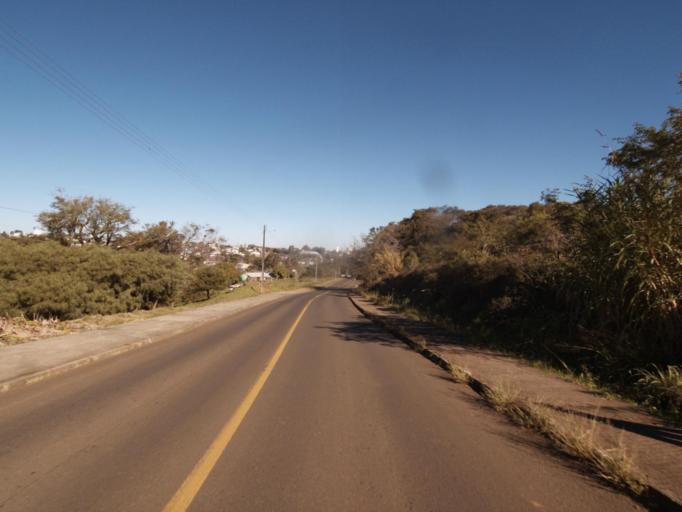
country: AR
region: Misiones
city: Bernardo de Irigoyen
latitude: -26.7098
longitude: -53.5265
